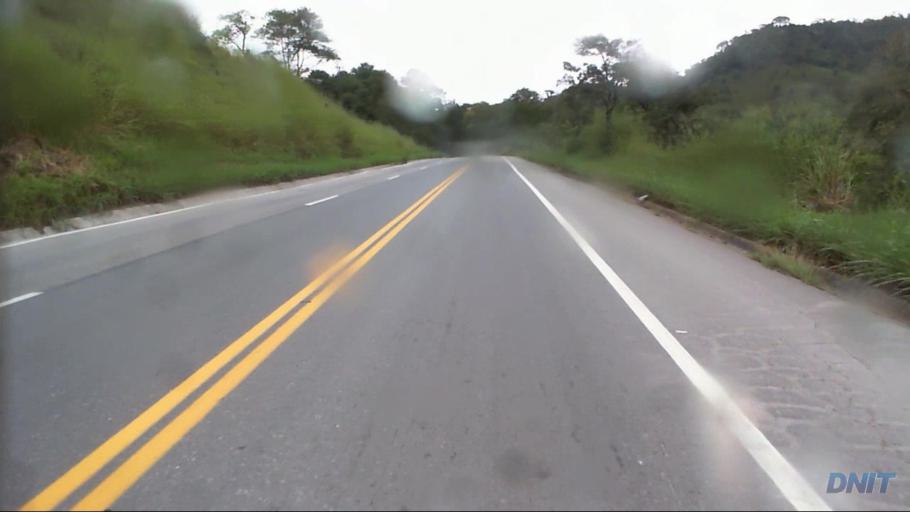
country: BR
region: Minas Gerais
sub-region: Nova Era
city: Nova Era
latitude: -19.7077
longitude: -42.9997
